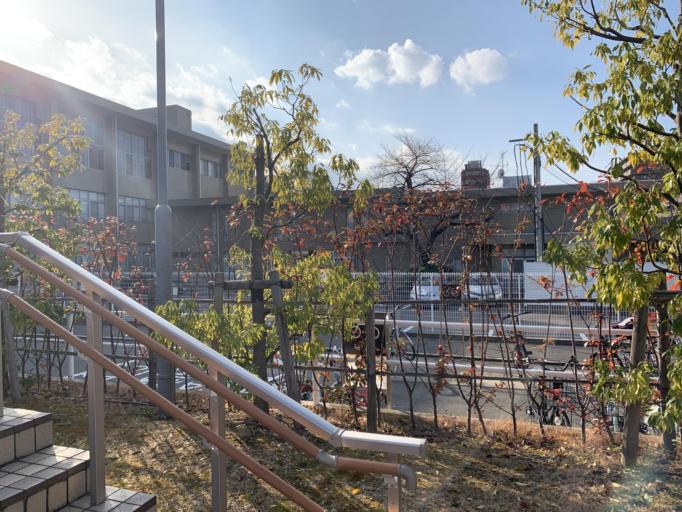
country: JP
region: Kyoto
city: Kyoto
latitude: 34.9977
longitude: 135.7345
